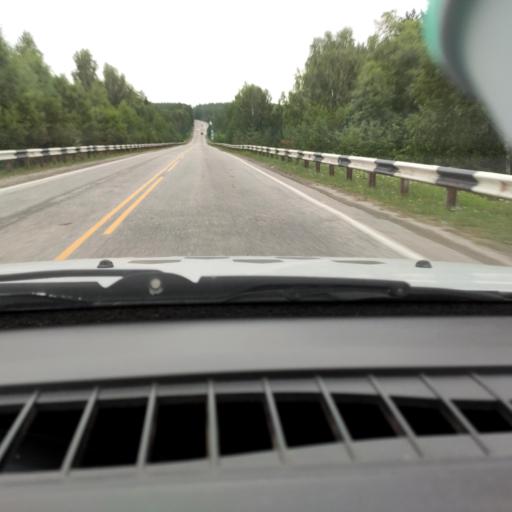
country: RU
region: Chelyabinsk
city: Kyshtym
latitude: 55.7321
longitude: 60.5266
